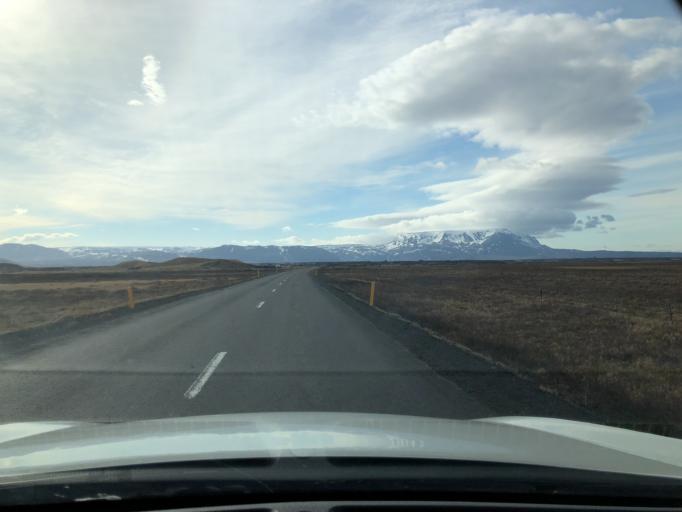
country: IS
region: Northeast
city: Laugar
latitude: 65.5591
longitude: -16.9929
